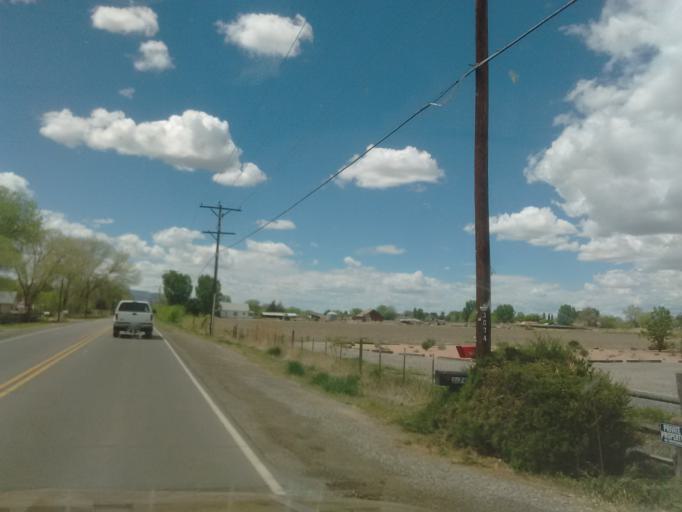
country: US
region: Colorado
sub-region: Mesa County
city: Fruitvale
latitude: 39.0774
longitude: -108.4820
